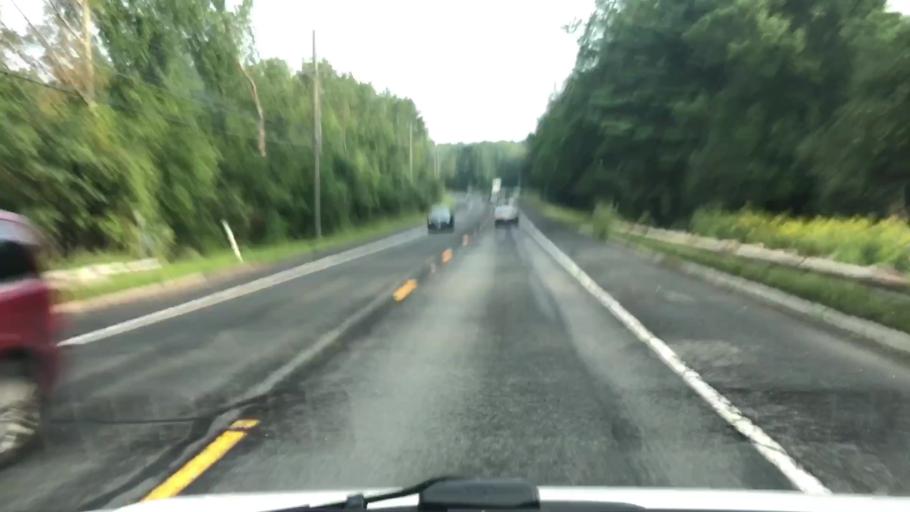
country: US
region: Massachusetts
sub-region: Berkshire County
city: Lanesborough
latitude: 42.5436
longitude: -73.2317
